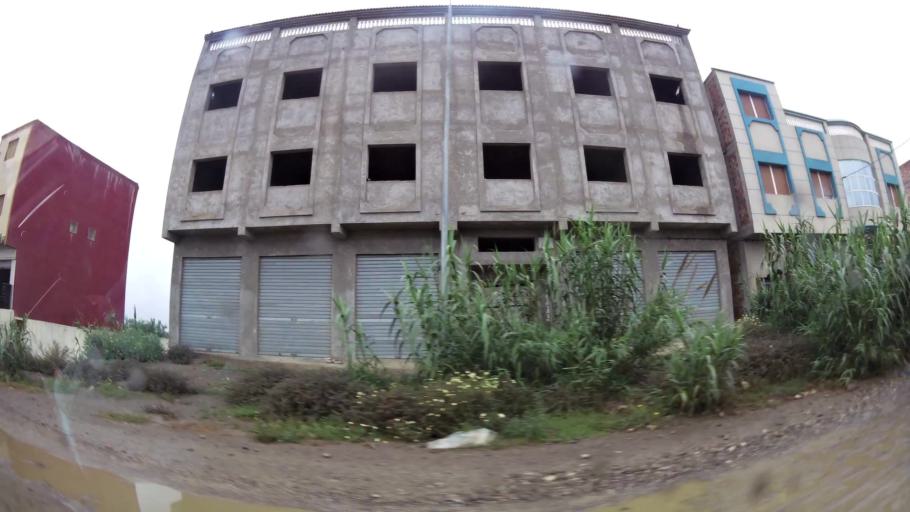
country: MA
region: Taza-Al Hoceima-Taounate
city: Imzourene
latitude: 35.1540
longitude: -3.8279
